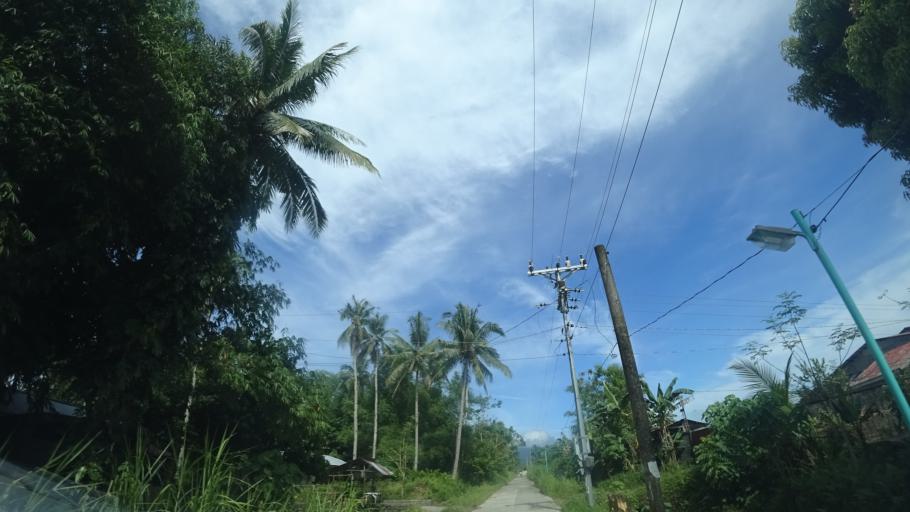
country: PH
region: Eastern Visayas
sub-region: Province of Leyte
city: Liberty
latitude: 10.8588
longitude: 124.9907
